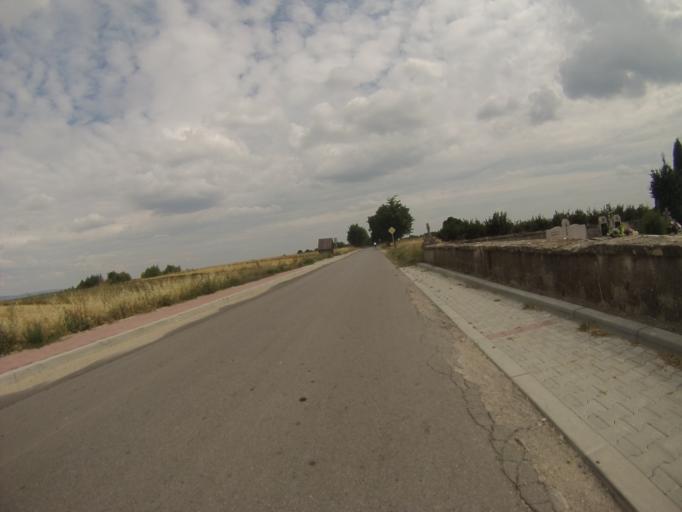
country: PL
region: Swietokrzyskie
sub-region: Powiat kielecki
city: Lagow
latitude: 50.7301
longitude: 21.1046
